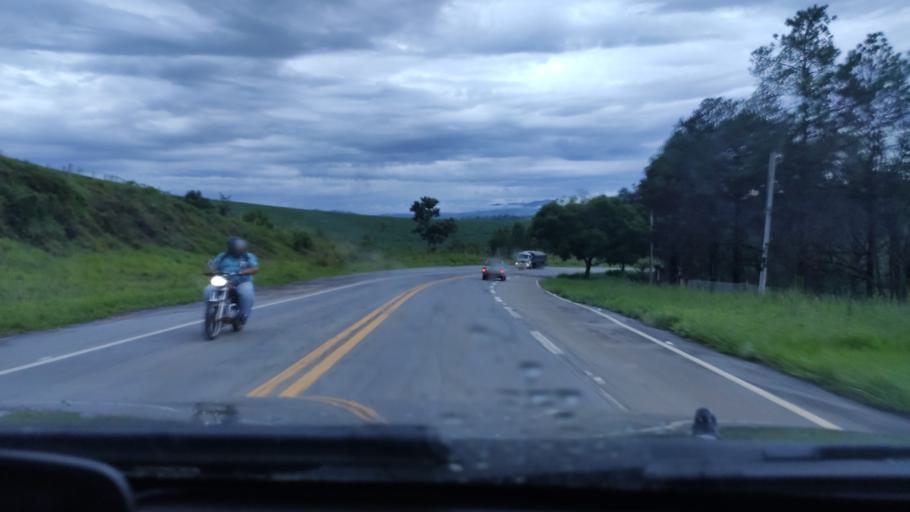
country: BR
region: Sao Paulo
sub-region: Socorro
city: Socorro
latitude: -22.6645
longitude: -46.5539
